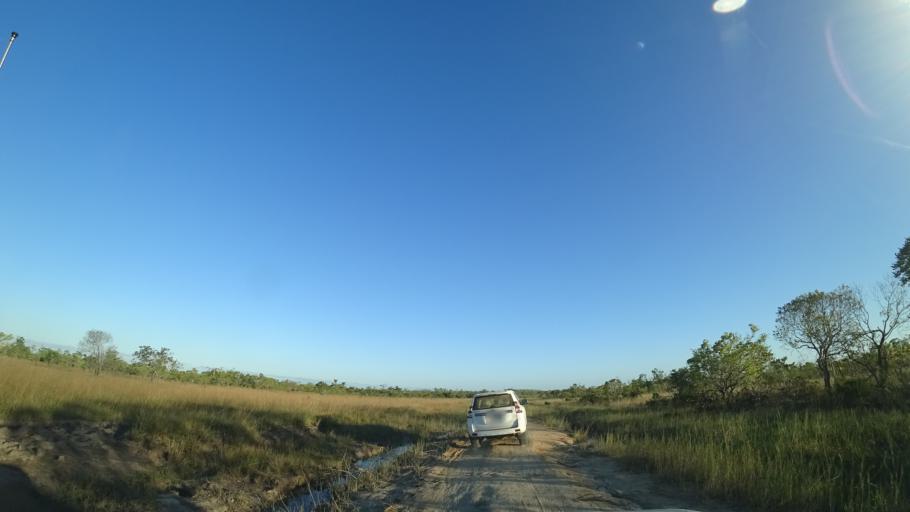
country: MZ
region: Sofala
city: Dondo
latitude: -19.5812
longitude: 35.0869
